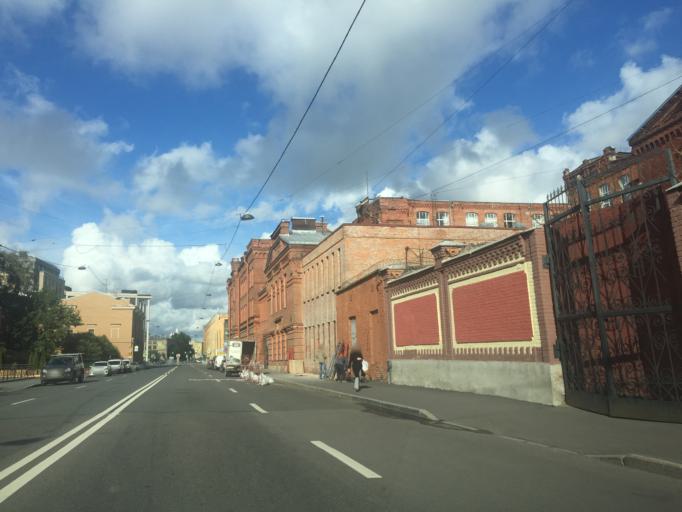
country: RU
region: St.-Petersburg
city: Centralniy
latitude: 59.9356
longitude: 30.3856
